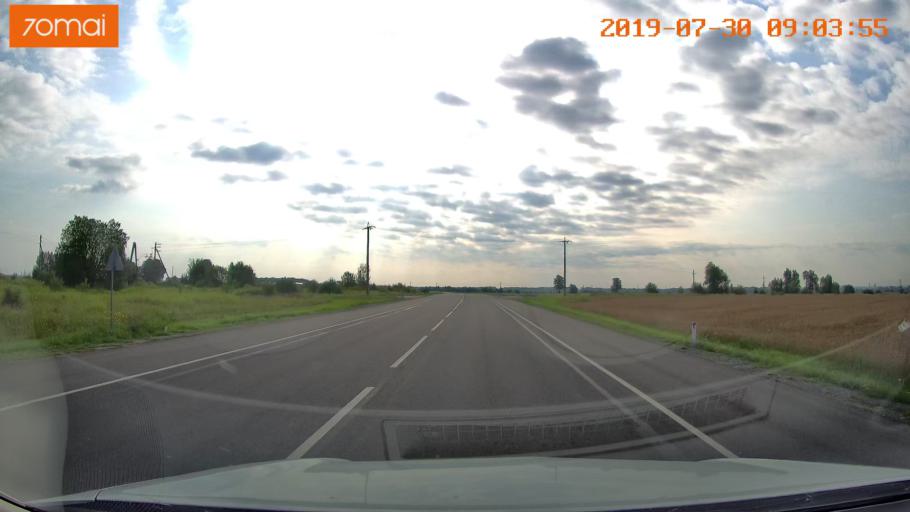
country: RU
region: Kaliningrad
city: Gusev
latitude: 54.6054
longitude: 22.2662
